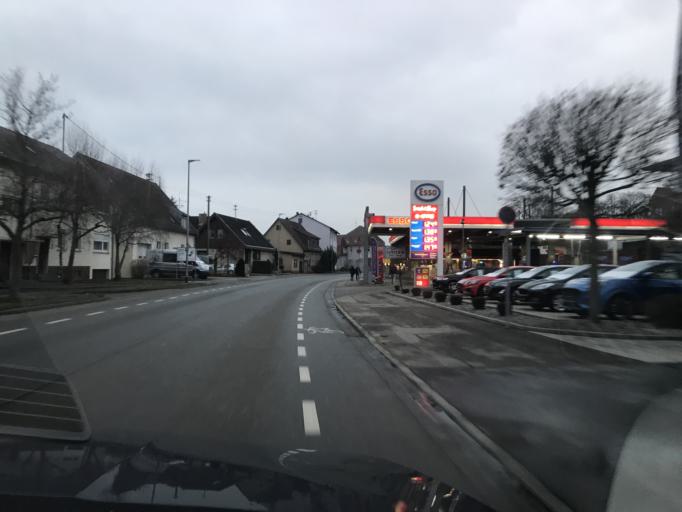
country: DE
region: Baden-Wuerttemberg
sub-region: Regierungsbezirk Stuttgart
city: Kongen
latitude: 48.6828
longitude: 9.3706
